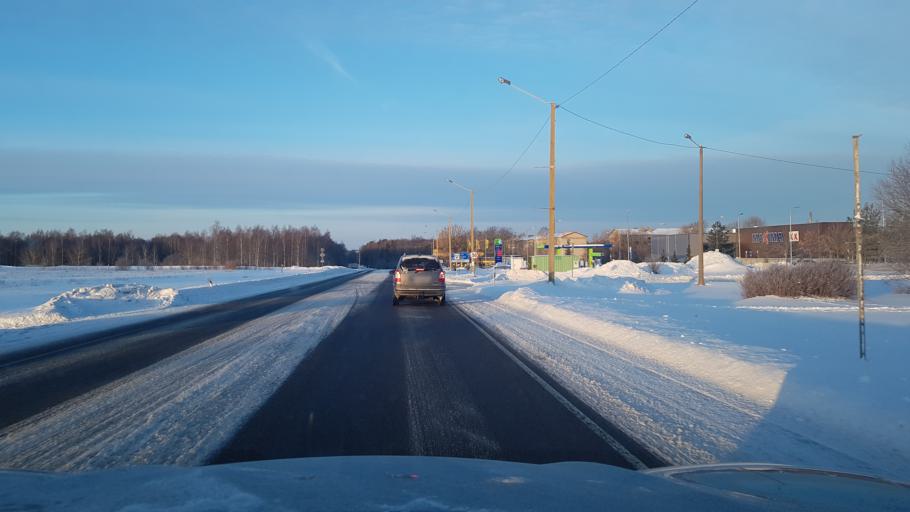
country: EE
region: Ida-Virumaa
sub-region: Sillamaee linn
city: Sillamae
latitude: 59.3904
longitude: 27.7781
